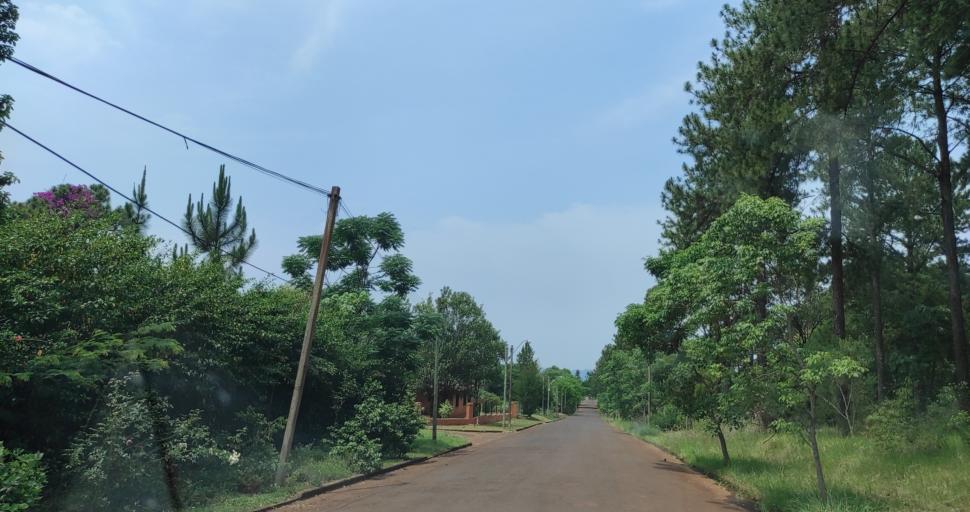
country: AR
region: Misiones
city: Ruiz de Montoya
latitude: -26.9695
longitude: -55.0611
